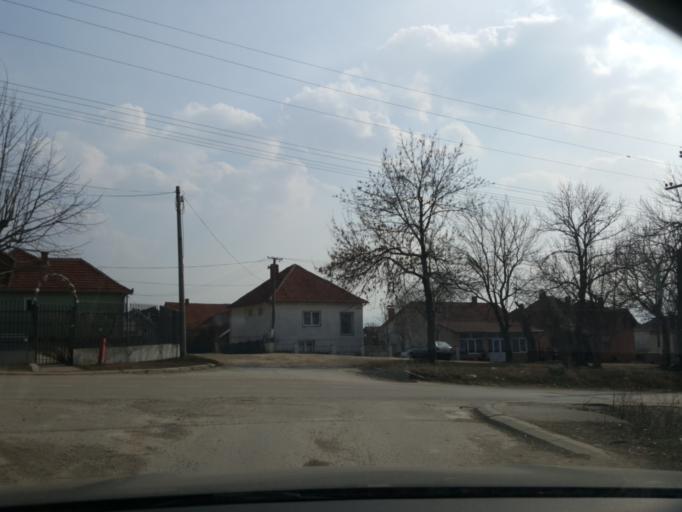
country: RS
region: Central Serbia
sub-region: Nisavski Okrug
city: Aleksinac
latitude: 43.5353
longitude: 21.7174
